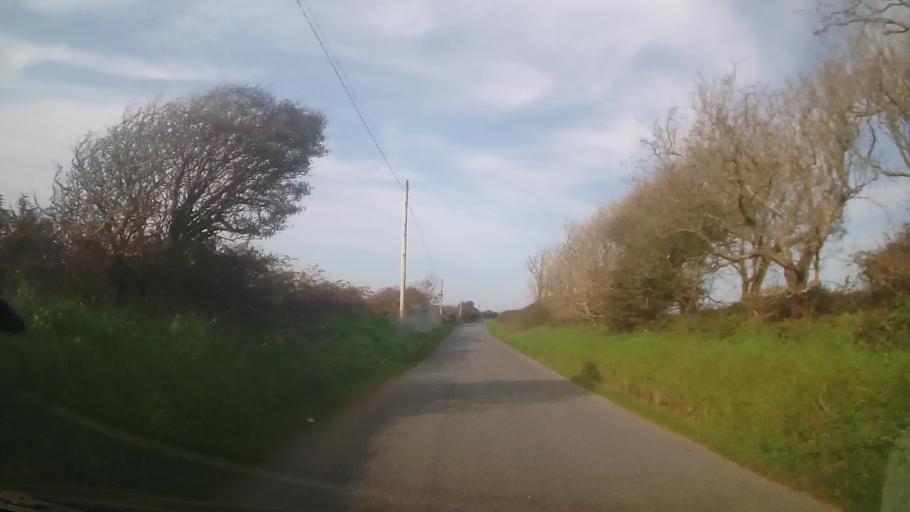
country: GB
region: Wales
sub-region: Pembrokeshire
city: Camrose
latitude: 51.8640
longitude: -5.0528
